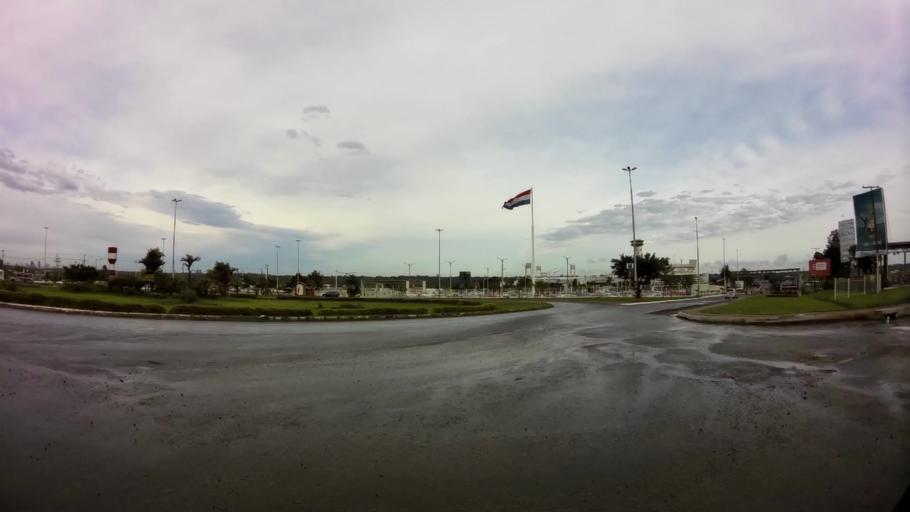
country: PY
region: Central
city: Limpio
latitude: -25.2437
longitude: -57.5111
